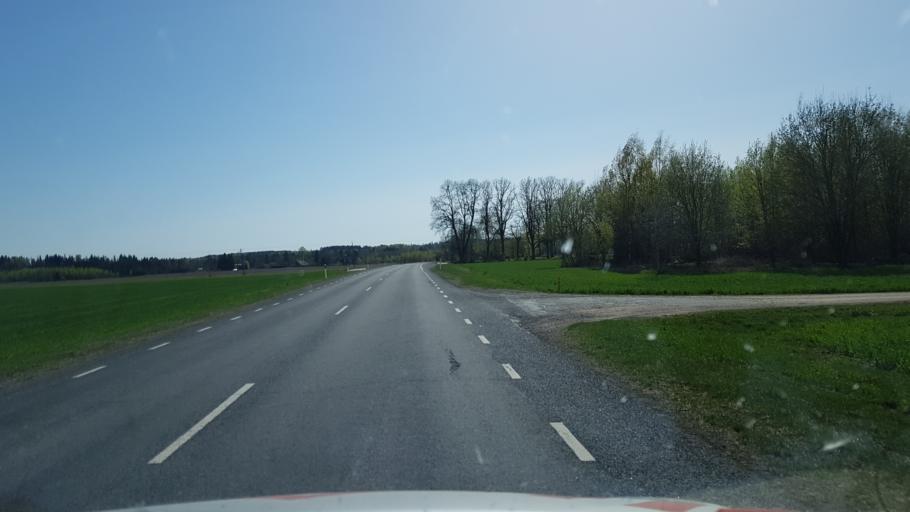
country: EE
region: Viljandimaa
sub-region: Viljandi linn
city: Viljandi
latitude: 58.3156
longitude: 25.5649
